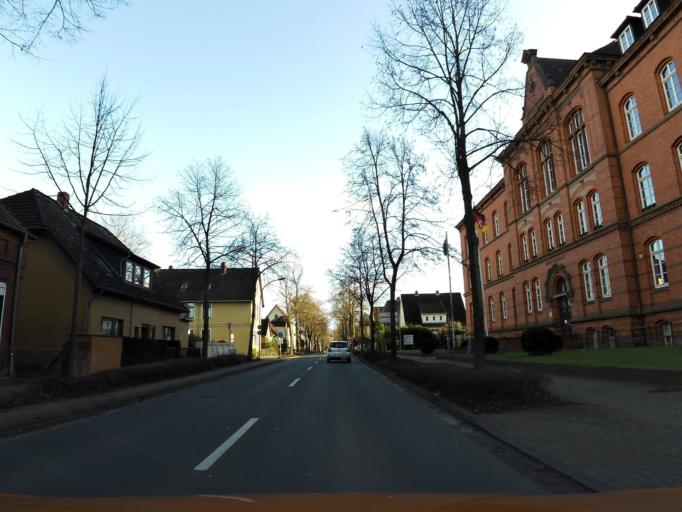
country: DE
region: Lower Saxony
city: Verden
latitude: 52.9138
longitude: 9.2356
